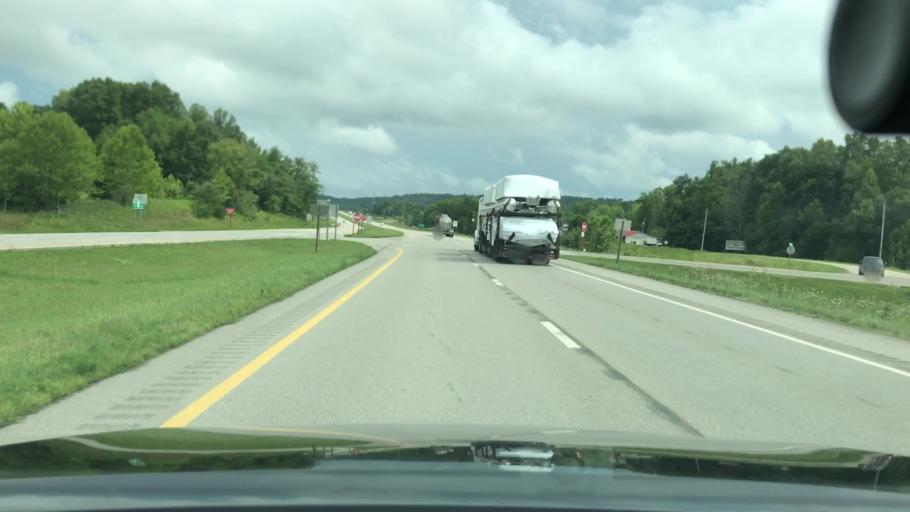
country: US
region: Ohio
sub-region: Jackson County
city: Oak Hill
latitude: 38.8962
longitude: -82.4389
